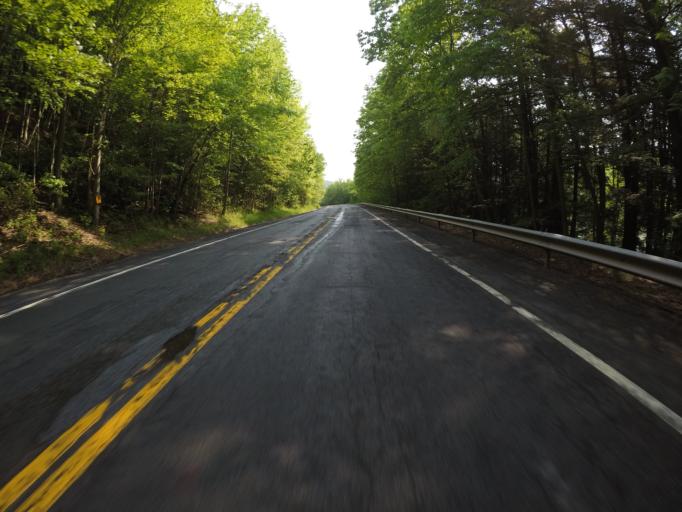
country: US
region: New York
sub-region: Sullivan County
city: Livingston Manor
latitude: 42.1105
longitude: -74.7771
